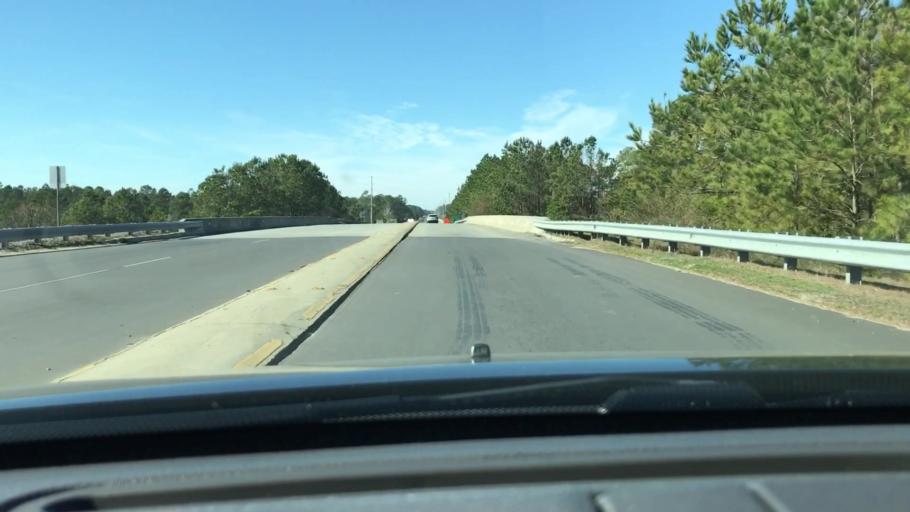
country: US
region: North Carolina
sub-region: Brunswick County
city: Shallotte
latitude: 33.9761
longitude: -78.4042
